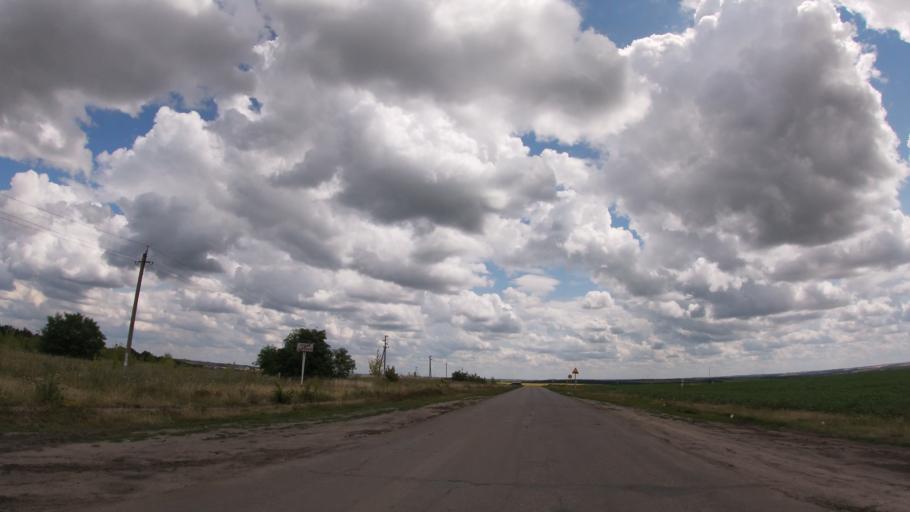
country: RU
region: Belgorod
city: Mayskiy
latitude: 50.5030
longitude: 36.4406
